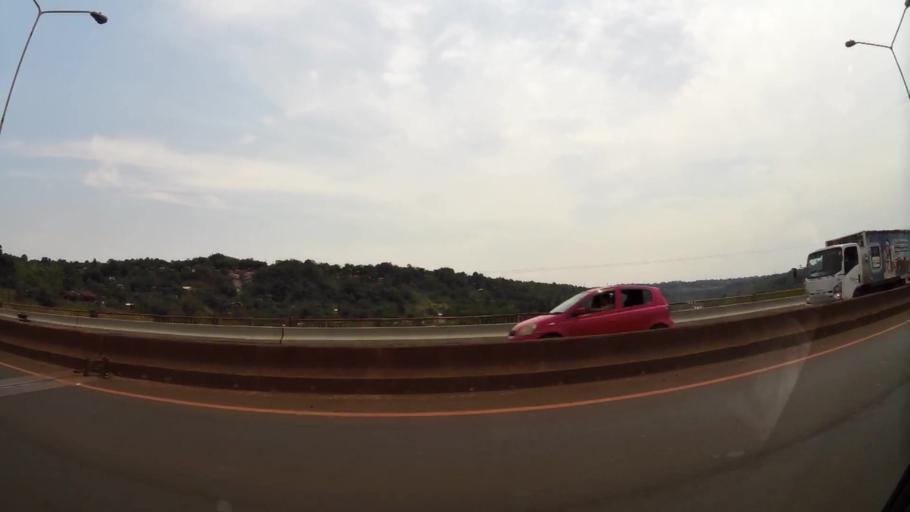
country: PY
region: Alto Parana
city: Ciudad del Este
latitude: -25.4905
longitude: -54.6309
